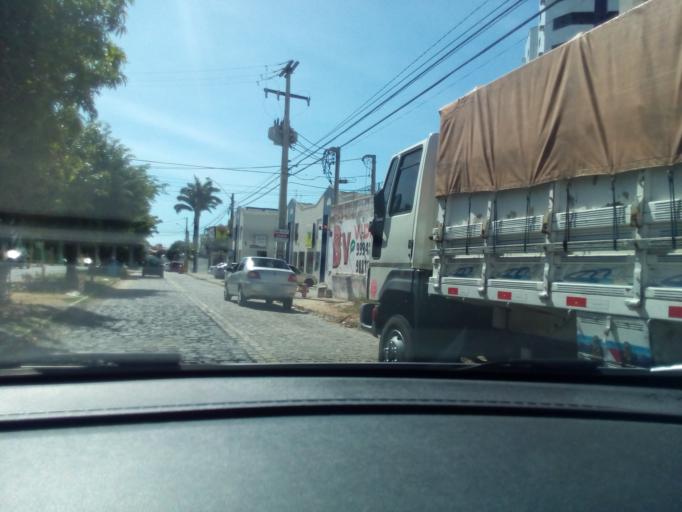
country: BR
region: Rio Grande do Norte
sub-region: Parnamirim
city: Parnamirim
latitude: -5.8877
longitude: -35.1973
